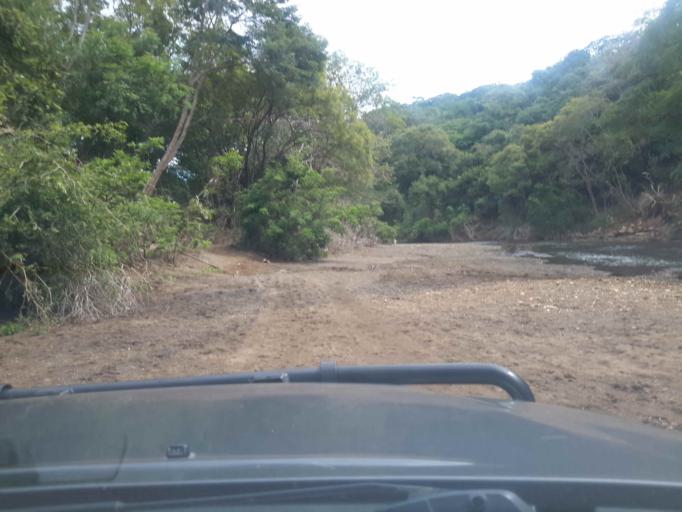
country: NI
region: Carazo
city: Santa Teresa
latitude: 11.6950
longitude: -86.2948
